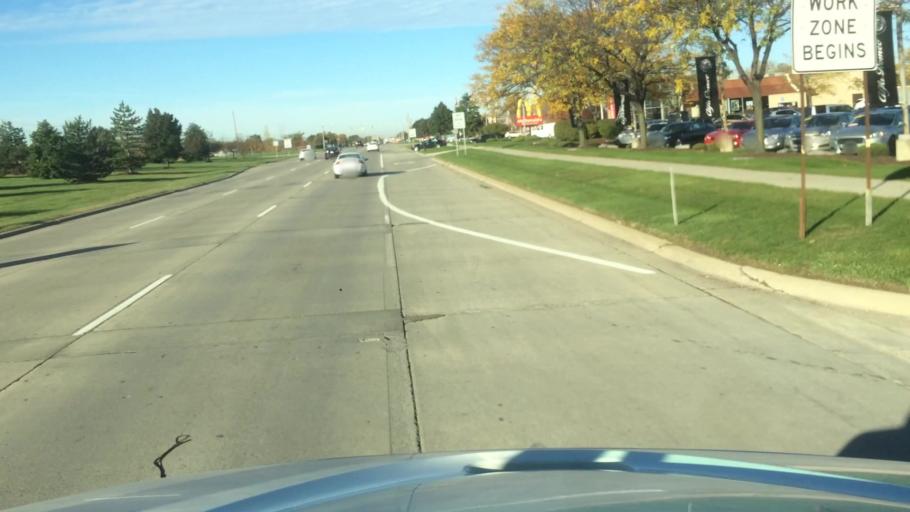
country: US
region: Michigan
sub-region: Macomb County
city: Clinton
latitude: 42.6285
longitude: -82.9403
